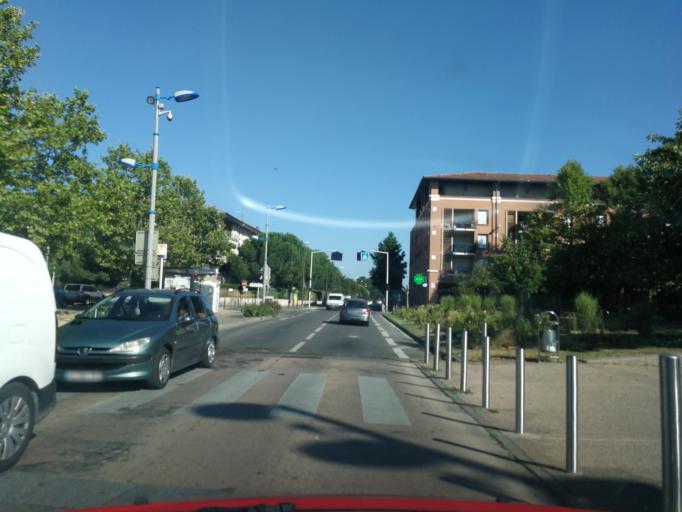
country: FR
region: Midi-Pyrenees
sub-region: Departement de la Haute-Garonne
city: Toulouse
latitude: 43.6292
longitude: 1.4494
